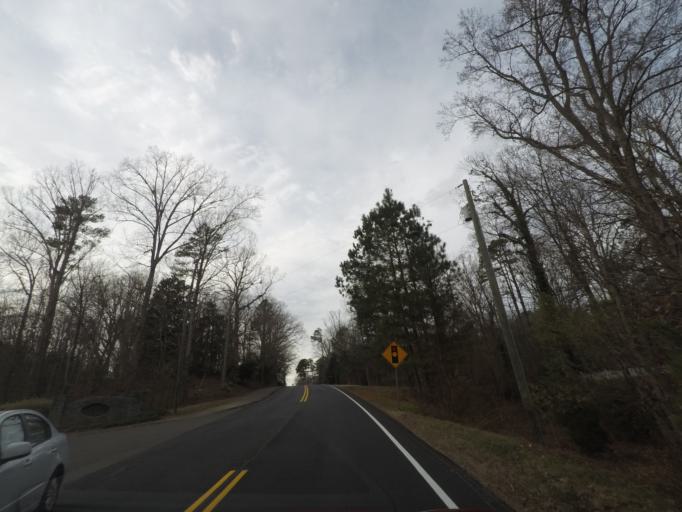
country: US
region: North Carolina
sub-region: Durham County
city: Durham
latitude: 36.0426
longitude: -78.9546
